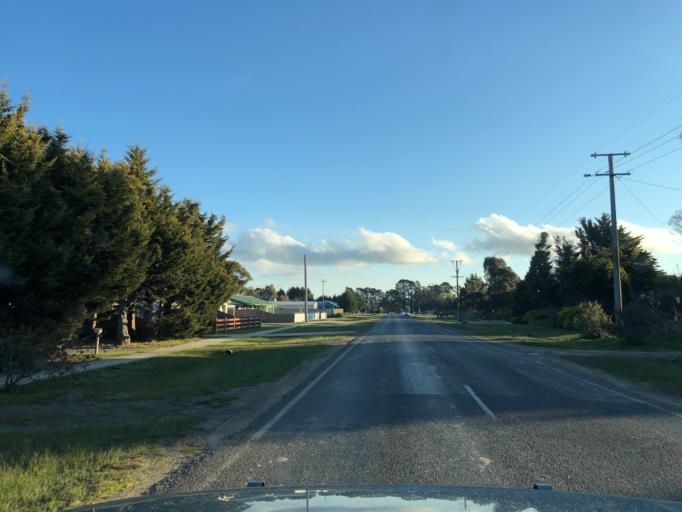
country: AU
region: Victoria
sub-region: Moorabool
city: Bacchus Marsh
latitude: -37.5935
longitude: 144.2342
